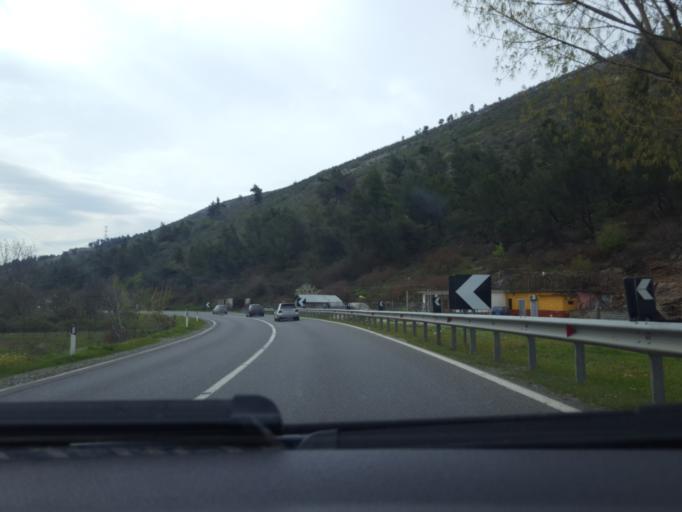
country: AL
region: Lezhe
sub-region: Rrethi i Lezhes
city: Balldreni i Ri
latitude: 41.8021
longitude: 19.6303
